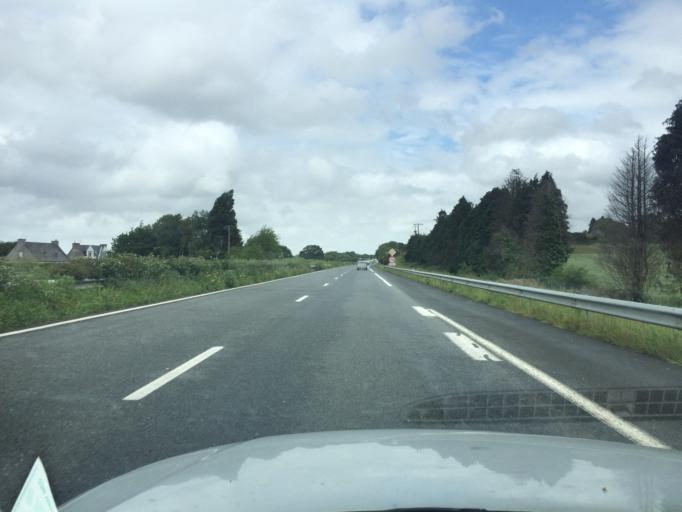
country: FR
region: Brittany
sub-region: Departement du Finistere
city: Bodilis
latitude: 48.5121
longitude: -4.0951
